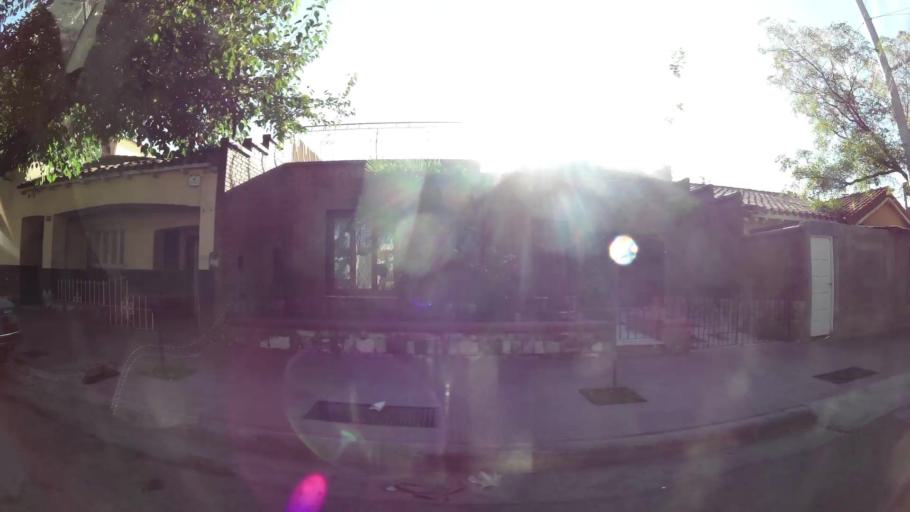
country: AR
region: Mendoza
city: Mendoza
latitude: -32.9013
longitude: -68.8288
